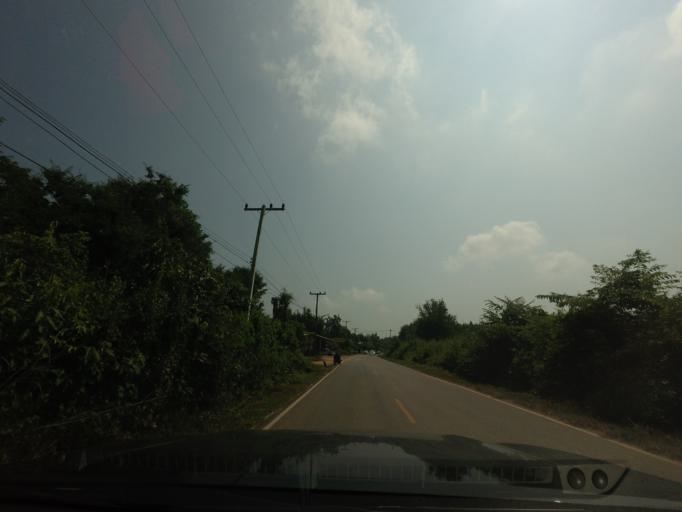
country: TH
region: Nan
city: Nan
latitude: 18.7742
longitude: 100.7378
